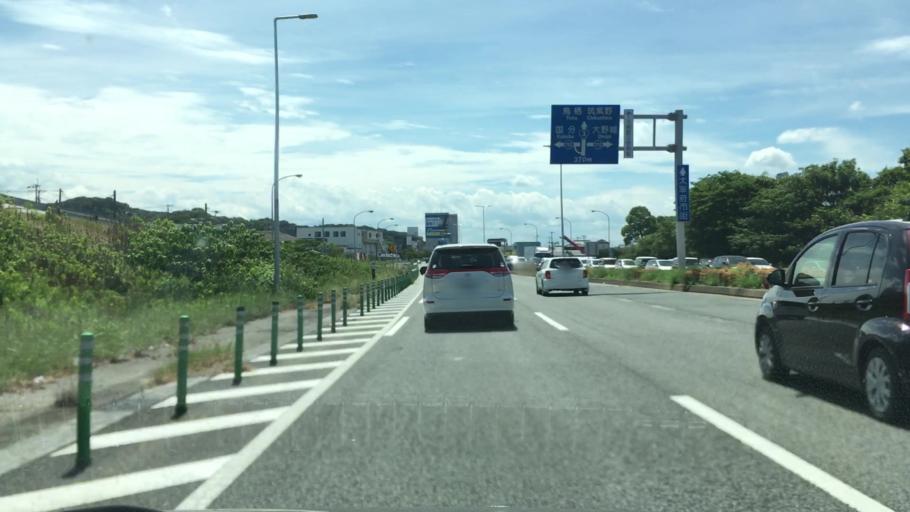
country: JP
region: Fukuoka
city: Onojo
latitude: 33.5308
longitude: 130.4921
